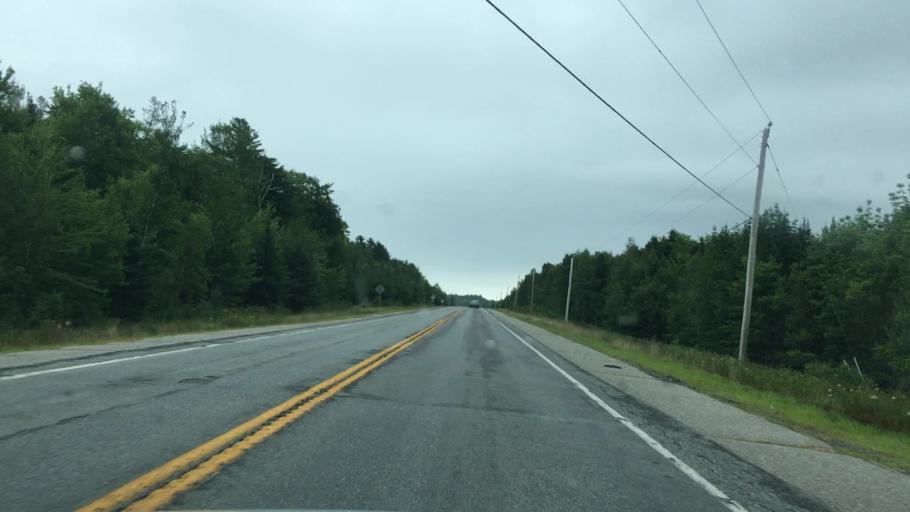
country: US
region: Maine
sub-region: Washington County
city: Cherryfield
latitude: 44.8560
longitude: -68.0526
